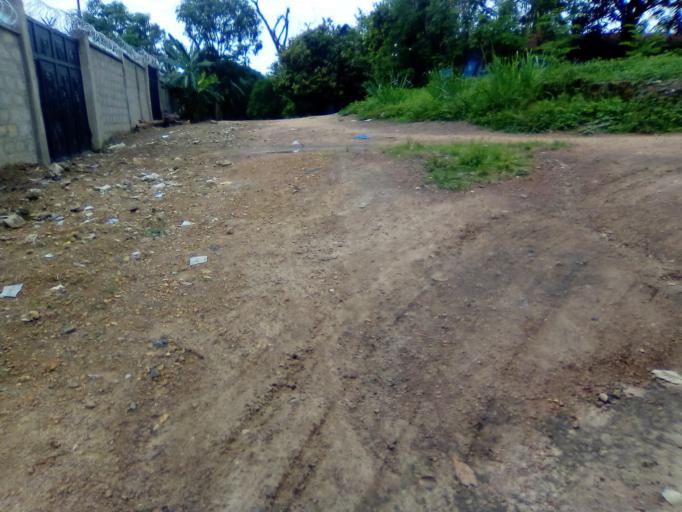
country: SL
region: Southern Province
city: Bo
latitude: 7.9471
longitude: -11.7101
